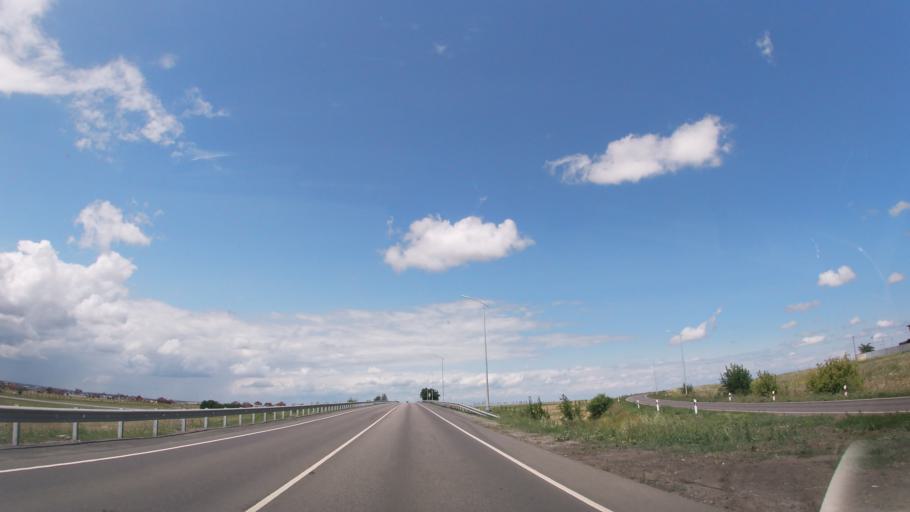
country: RU
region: Belgorod
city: Severnyy
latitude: 50.6736
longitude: 36.4765
